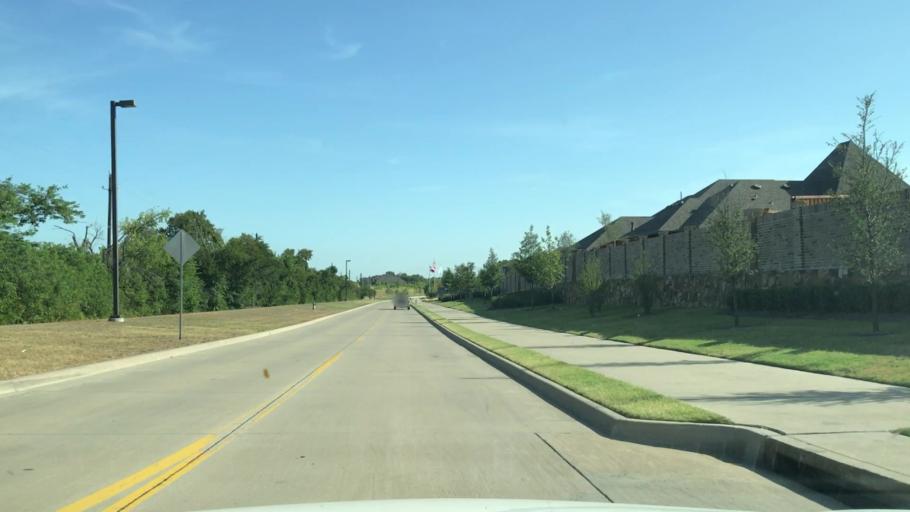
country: US
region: Texas
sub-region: Collin County
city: McKinney
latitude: 33.2337
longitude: -96.6518
